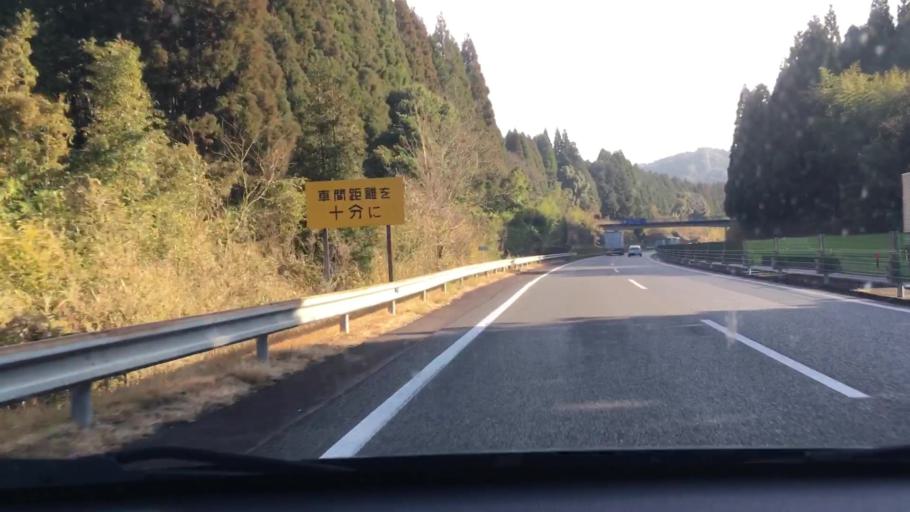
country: JP
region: Kagoshima
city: Okuchi-shinohara
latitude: 31.9997
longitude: 130.7583
